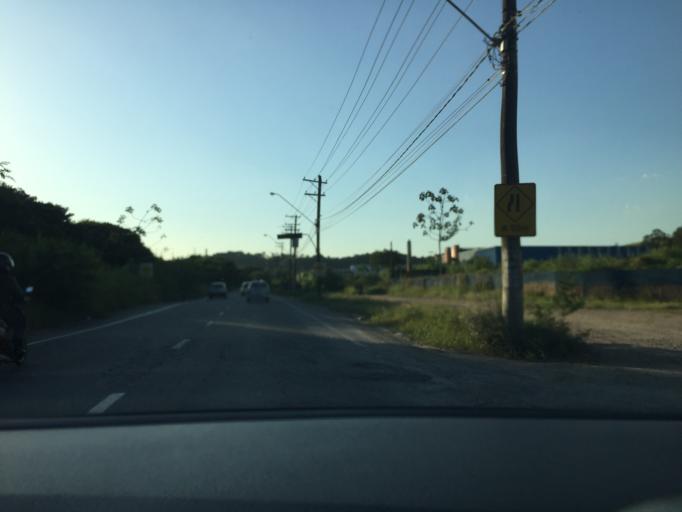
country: BR
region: Sao Paulo
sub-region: Varzea Paulista
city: Varzea Paulista
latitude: -23.2071
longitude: -46.8380
